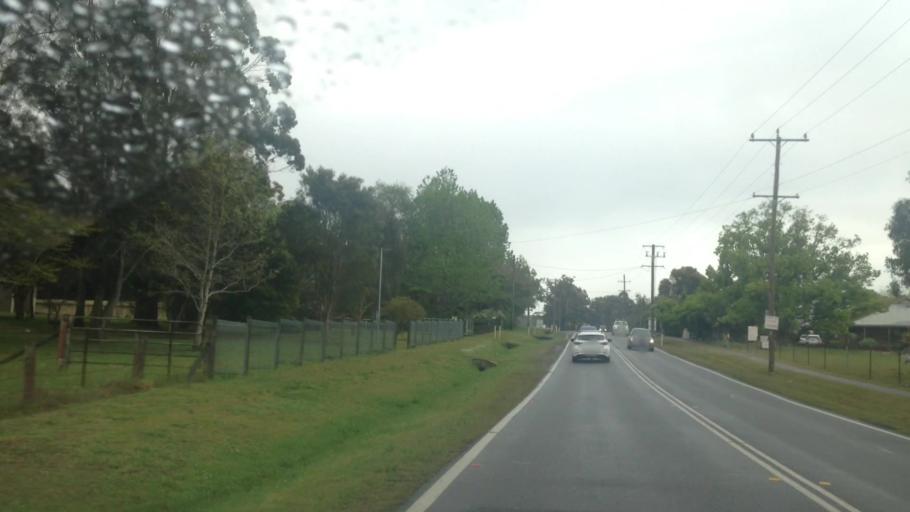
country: AU
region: New South Wales
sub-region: Wyong Shire
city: Charmhaven
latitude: -33.1713
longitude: 151.4777
